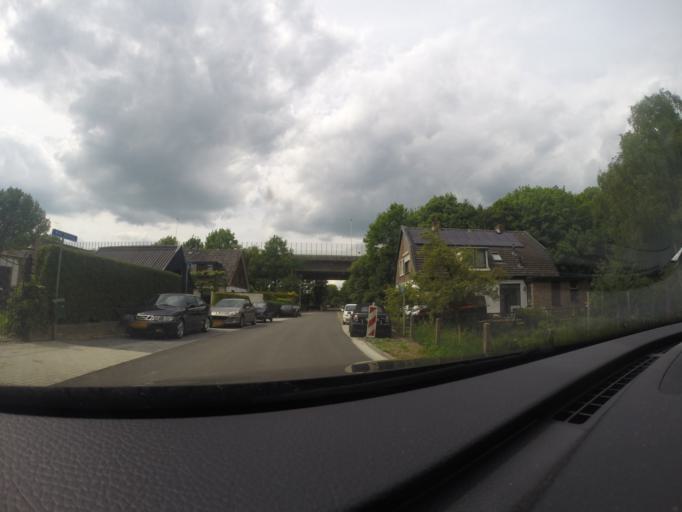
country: NL
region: Gelderland
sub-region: Gemeente Hattem
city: Hattem
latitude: 52.5007
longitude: 6.0584
